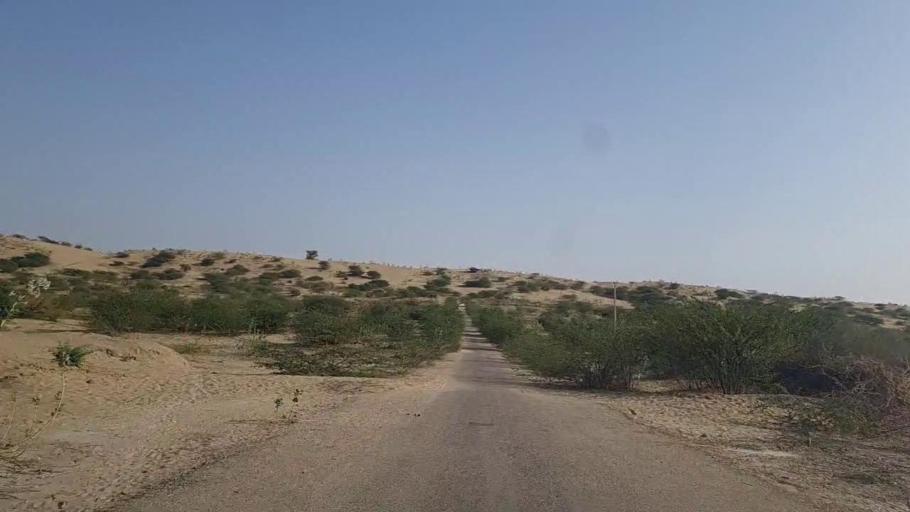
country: PK
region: Sindh
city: Naukot
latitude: 24.6206
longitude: 69.3712
